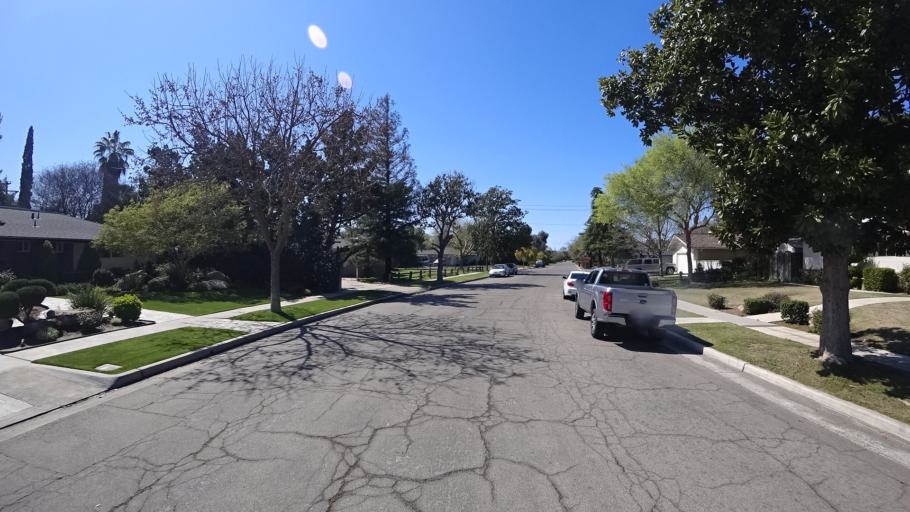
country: US
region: California
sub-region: Fresno County
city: Fresno
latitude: 36.8047
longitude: -119.8213
